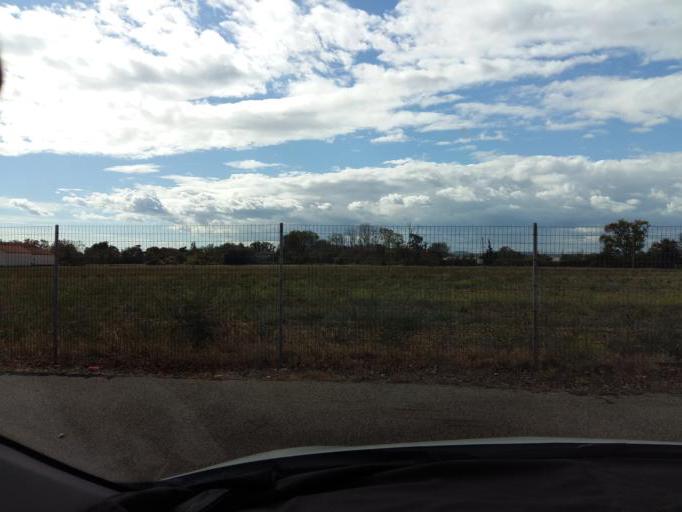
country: FR
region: Provence-Alpes-Cote d'Azur
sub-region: Departement du Vaucluse
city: Le Pontet
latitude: 43.9834
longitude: 4.8733
